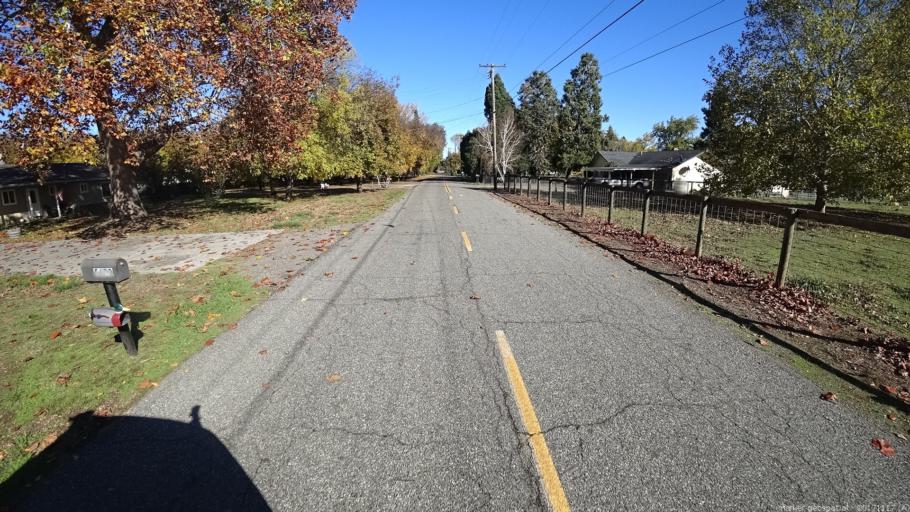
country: US
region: California
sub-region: Shasta County
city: Anderson
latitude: 40.4509
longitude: -122.2359
